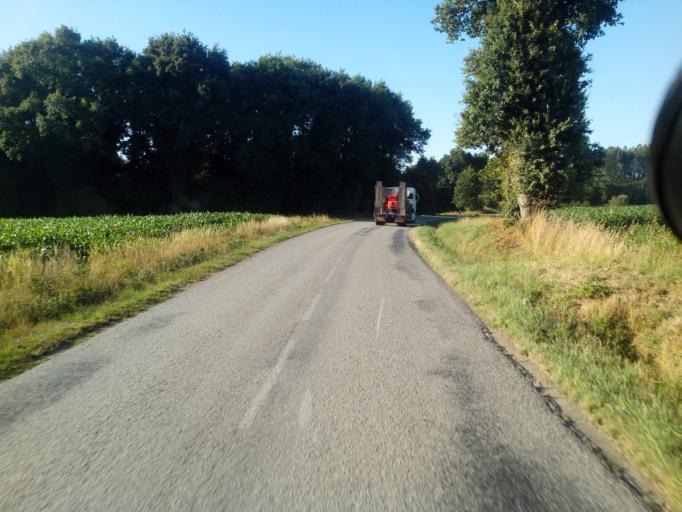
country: FR
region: Brittany
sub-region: Departement du Morbihan
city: Guilliers
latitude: 48.0346
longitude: -2.4045
